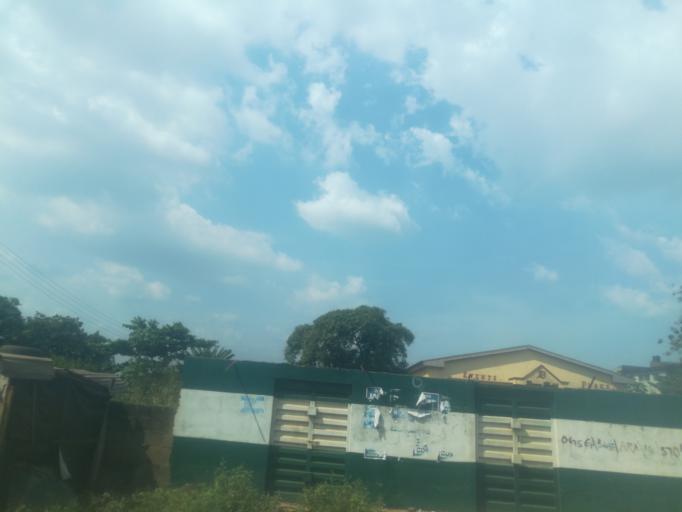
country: NG
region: Ogun
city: Abeokuta
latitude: 7.1736
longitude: 3.3762
